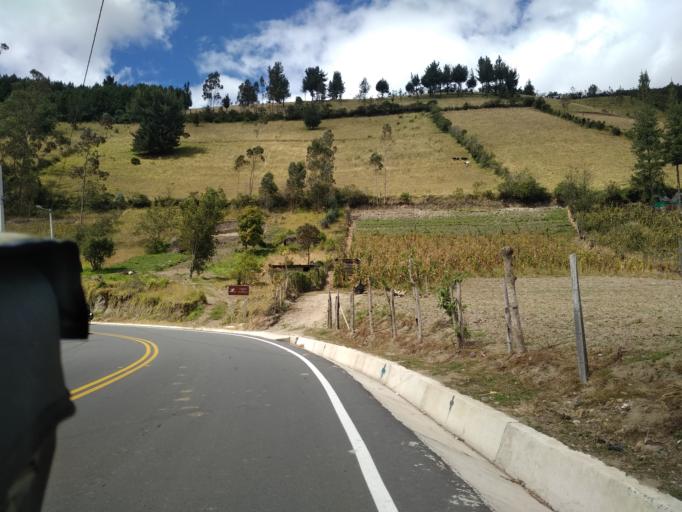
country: EC
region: Cotopaxi
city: Saquisili
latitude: -0.7073
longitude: -78.8861
